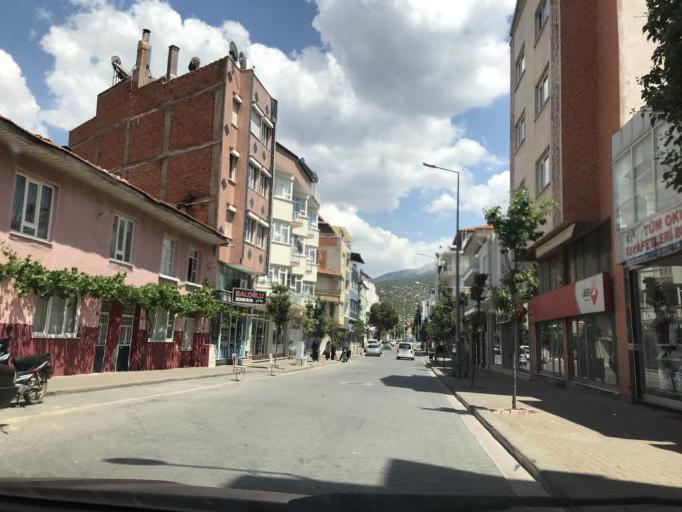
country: TR
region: Denizli
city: Tavas
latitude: 37.5735
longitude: 29.0691
